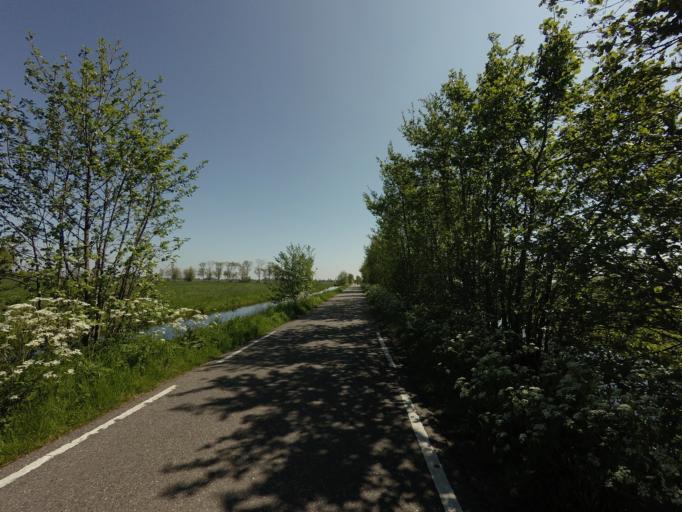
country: NL
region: South Holland
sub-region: Gemeente Gouda
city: Gouda
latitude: 51.9661
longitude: 4.6639
